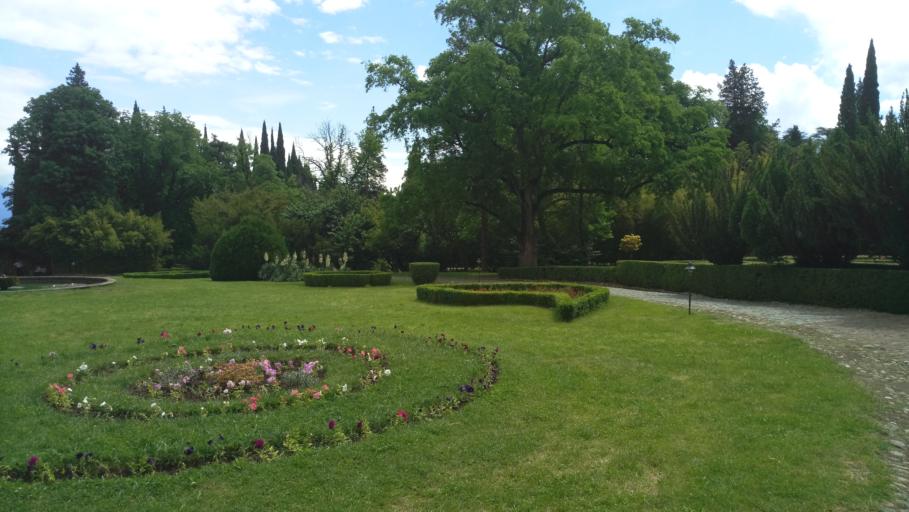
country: GE
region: Kakheti
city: Tsinandali
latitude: 41.8965
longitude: 45.5675
